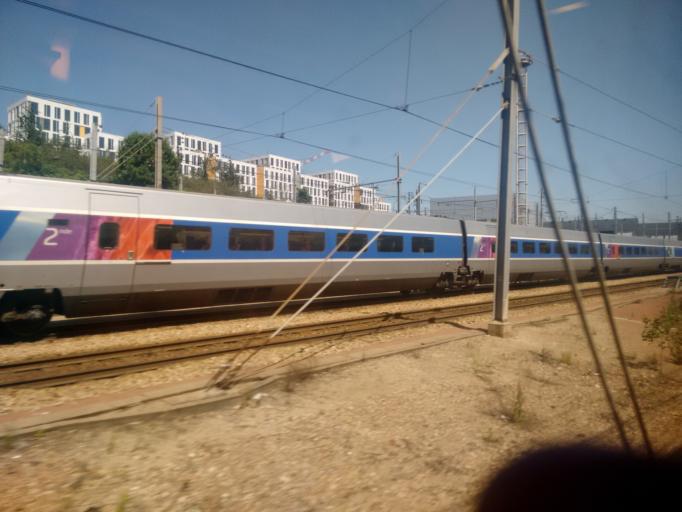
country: FR
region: Ile-de-France
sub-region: Departement des Hauts-de-Seine
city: Chatillon
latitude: 48.7980
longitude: 2.2968
